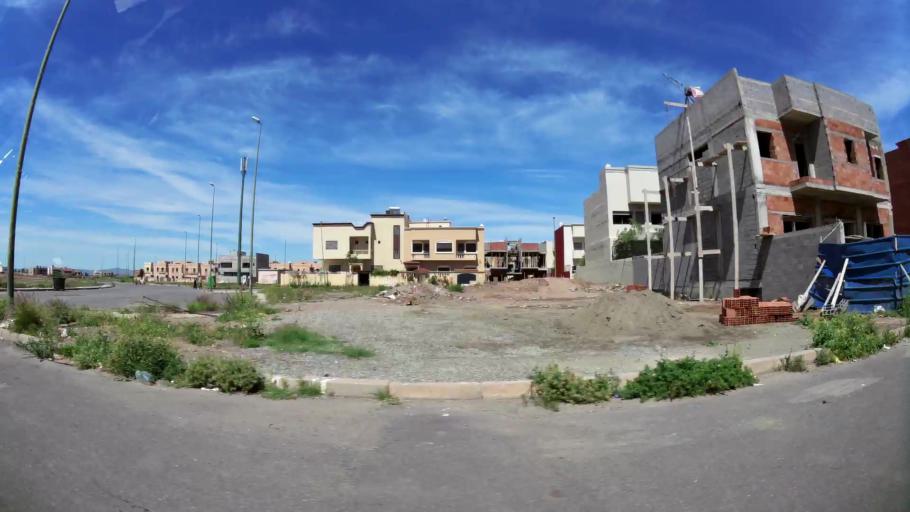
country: MA
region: Marrakech-Tensift-Al Haouz
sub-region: Marrakech
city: Marrakesh
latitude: 31.6488
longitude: -8.0739
